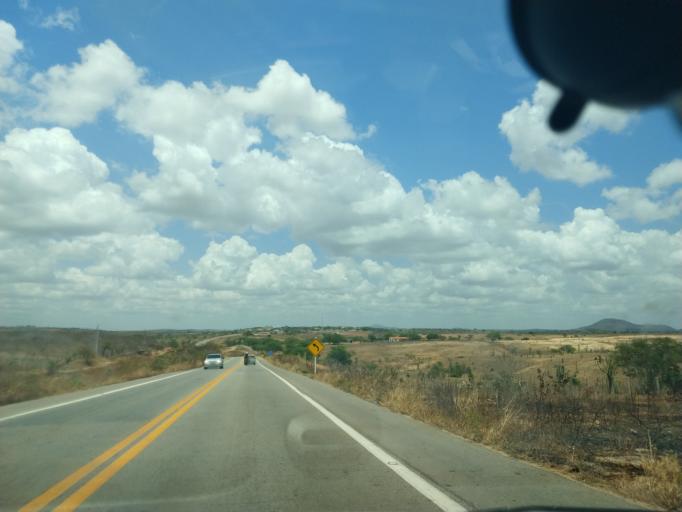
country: BR
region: Rio Grande do Norte
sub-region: Tangara
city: Tangara
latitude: -6.1830
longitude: -35.7743
